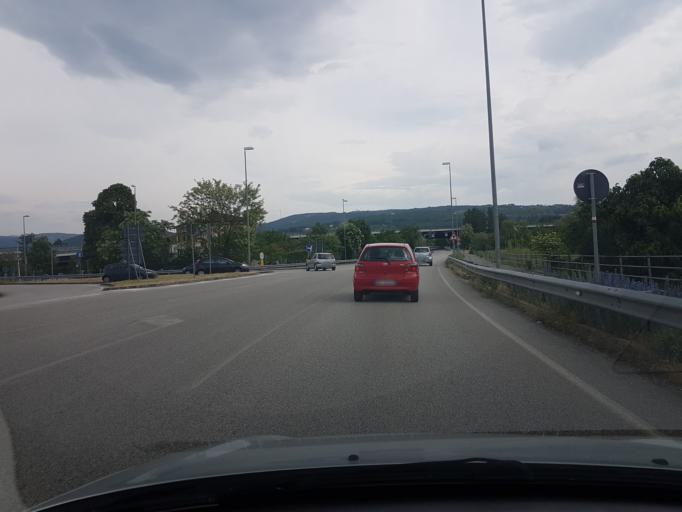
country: SI
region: Koper-Capodistria
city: Spodnje Skofije
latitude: 45.5907
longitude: 13.7971
